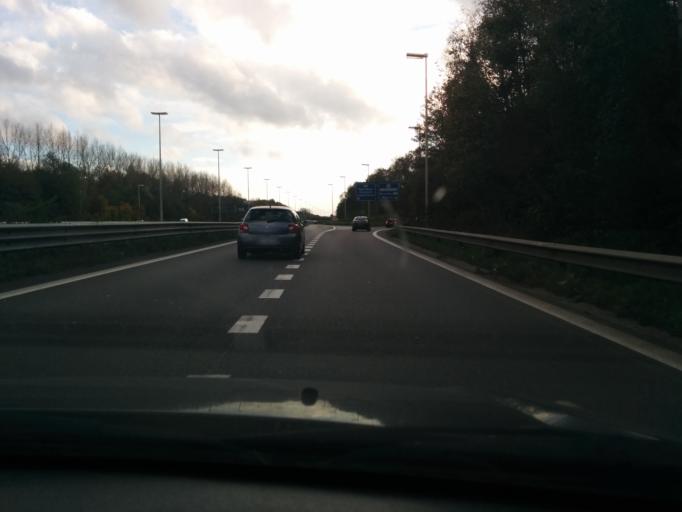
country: BE
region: Wallonia
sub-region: Province du Brabant Wallon
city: Braine-le-Chateau
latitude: 50.6599
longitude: 4.3101
